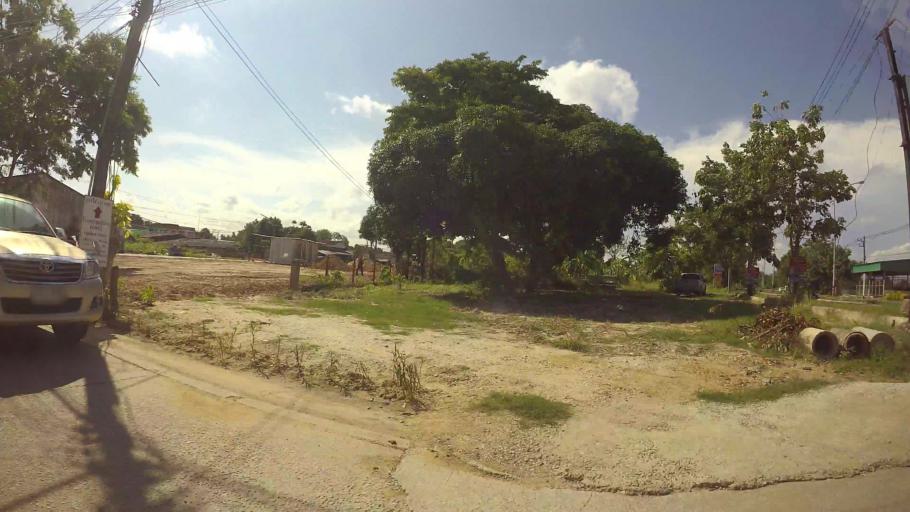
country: TH
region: Rayong
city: Rayong
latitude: 12.6729
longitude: 101.2943
